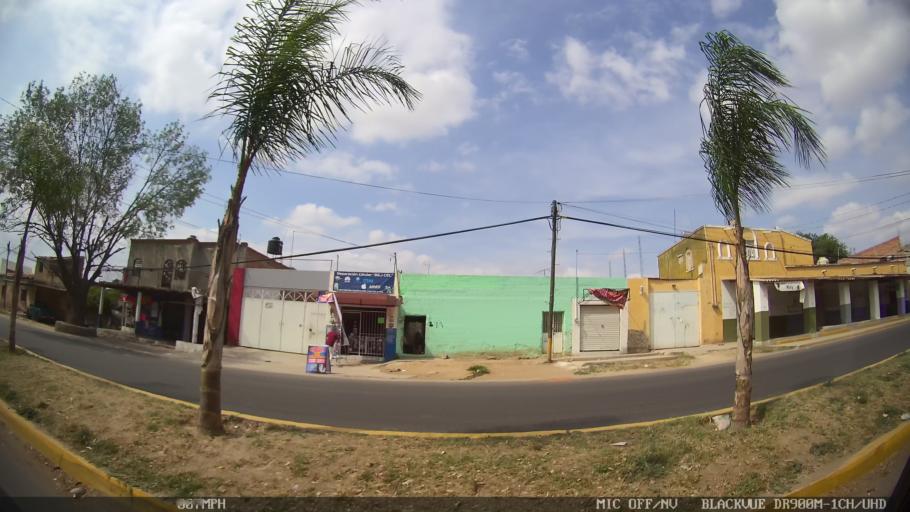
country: MX
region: Jalisco
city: Coyula
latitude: 20.6515
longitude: -103.2164
